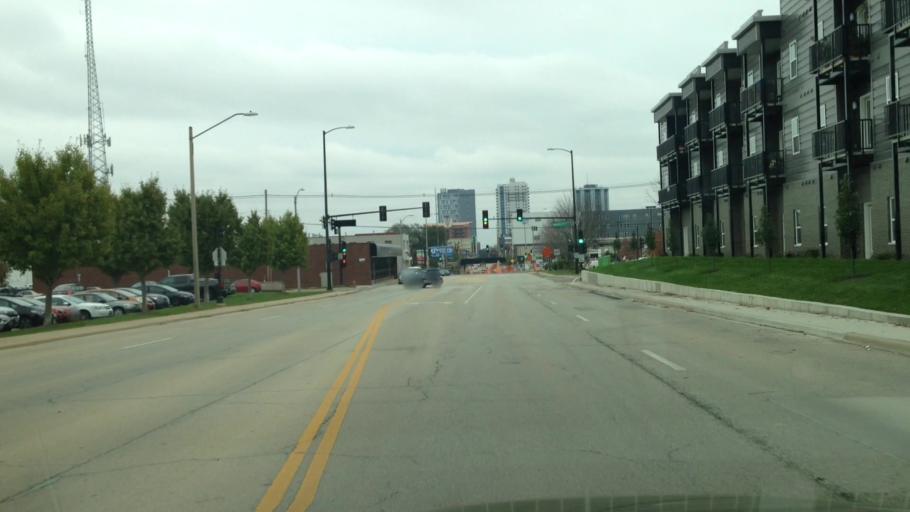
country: US
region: Illinois
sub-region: Champaign County
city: Champaign
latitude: 40.1101
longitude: -88.2462
